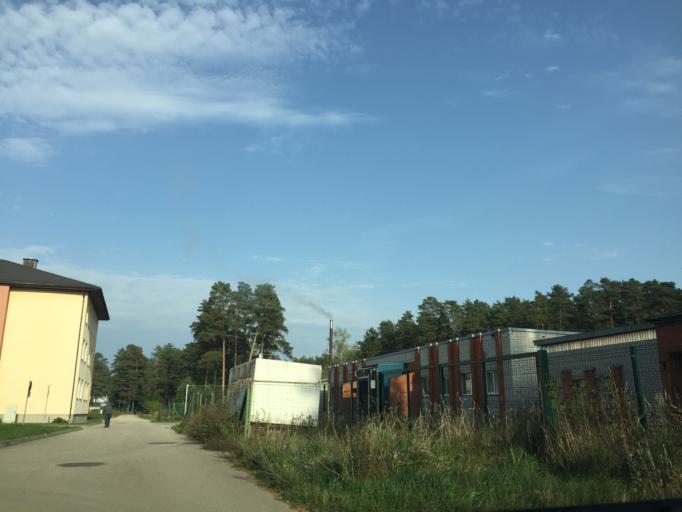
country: LV
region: Garkalne
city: Garkalne
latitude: 56.9603
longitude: 24.4274
